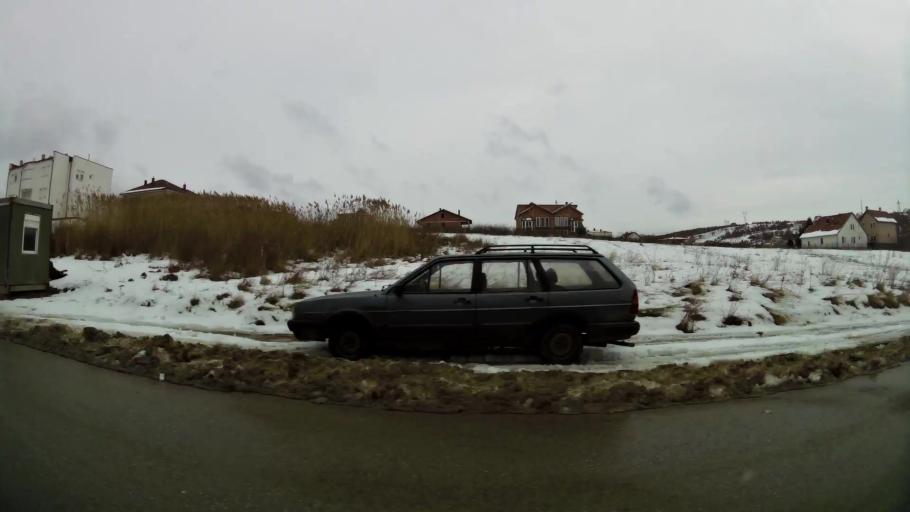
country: XK
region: Pristina
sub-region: Komuna e Prishtines
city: Pristina
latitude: 42.6437
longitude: 21.1818
